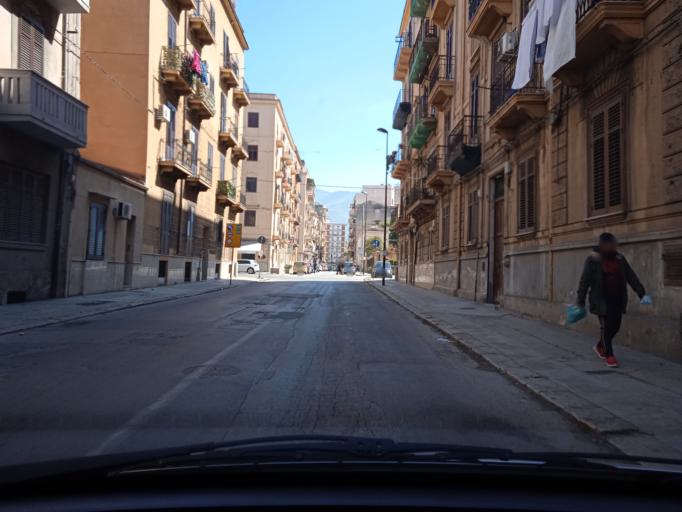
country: IT
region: Sicily
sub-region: Palermo
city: Palermo
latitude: 38.1083
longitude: 13.3602
